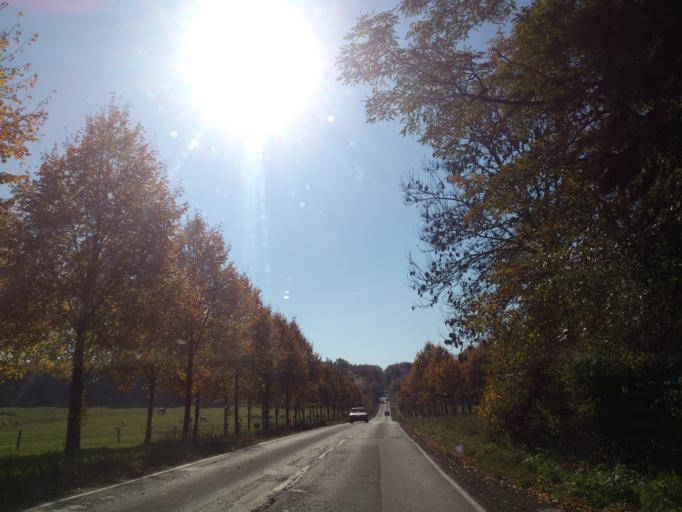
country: DE
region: Hesse
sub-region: Regierungsbezirk Kassel
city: Calden
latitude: 51.3906
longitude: 9.4165
